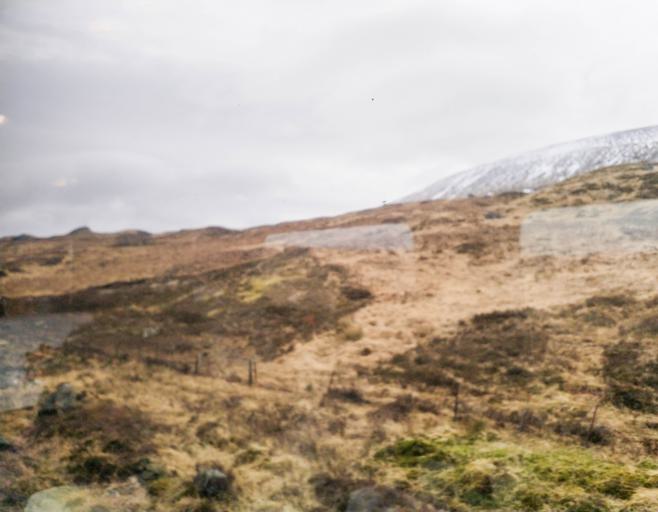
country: GB
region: Scotland
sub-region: Highland
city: Spean Bridge
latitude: 56.5851
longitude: -4.6658
